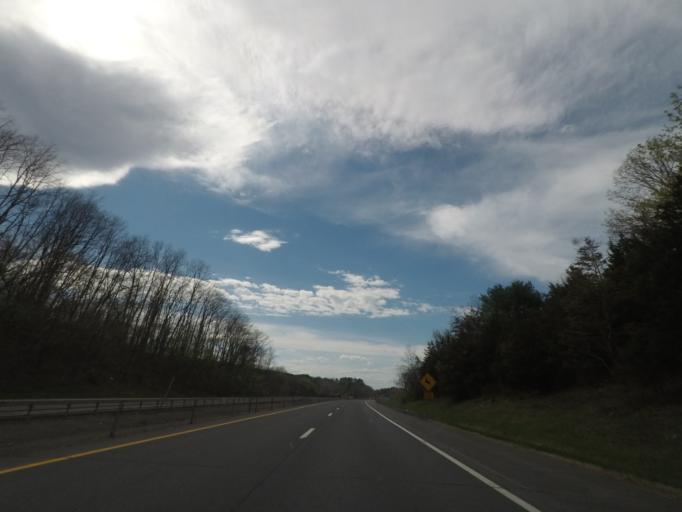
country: US
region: New York
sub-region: Greene County
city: Jefferson Heights
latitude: 42.2503
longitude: -73.9017
